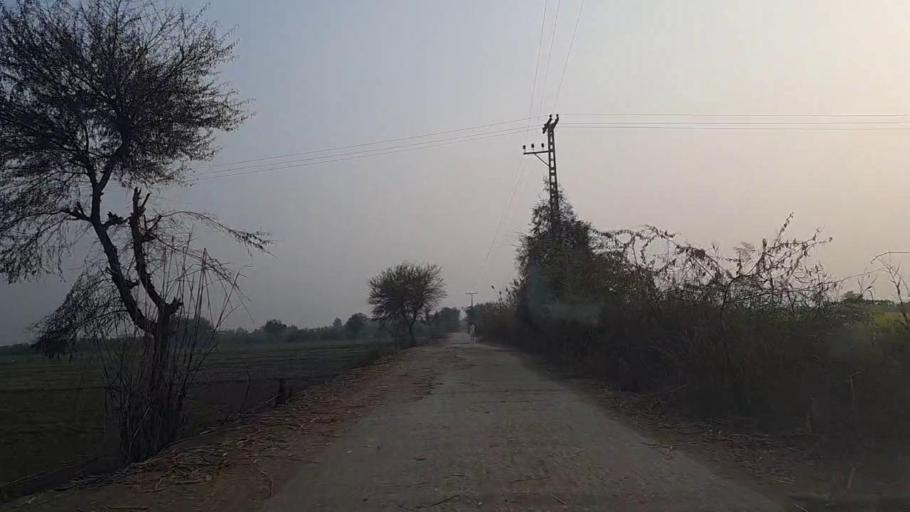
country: PK
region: Sindh
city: Sinjhoro
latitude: 26.1090
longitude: 68.7966
